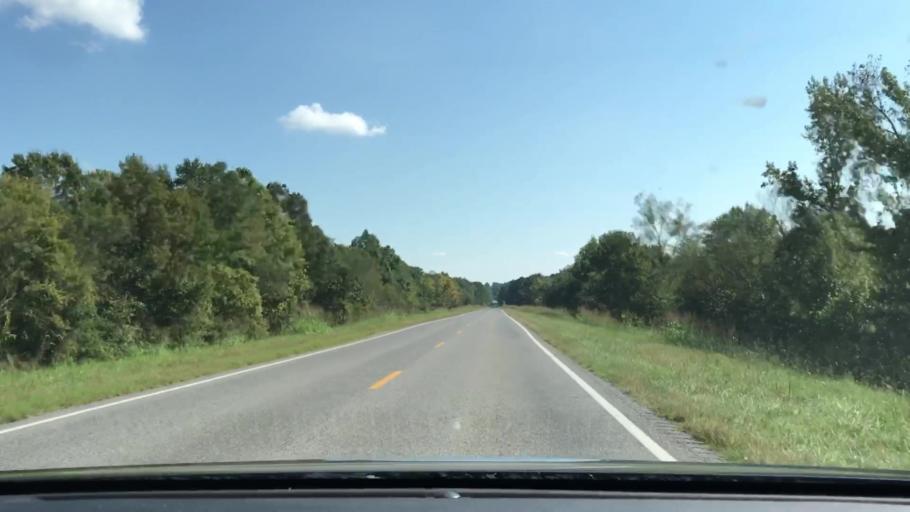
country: US
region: Kentucky
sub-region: Marshall County
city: Benton
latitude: 36.7647
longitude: -88.2366
